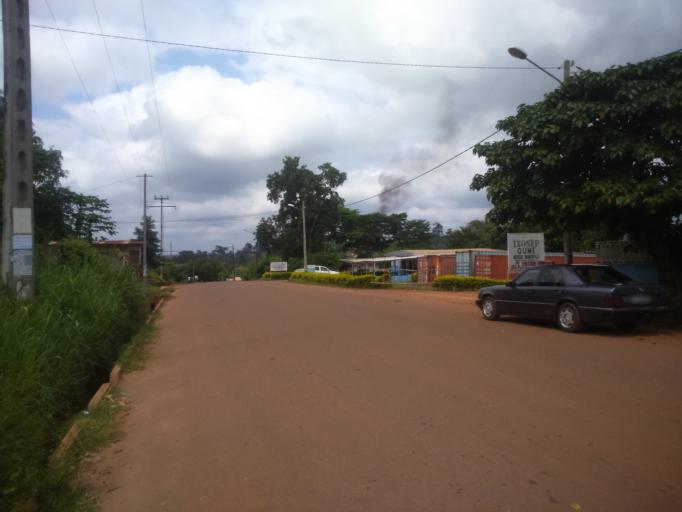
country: CI
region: Fromager
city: Oume
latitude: 6.3779
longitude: -5.4190
